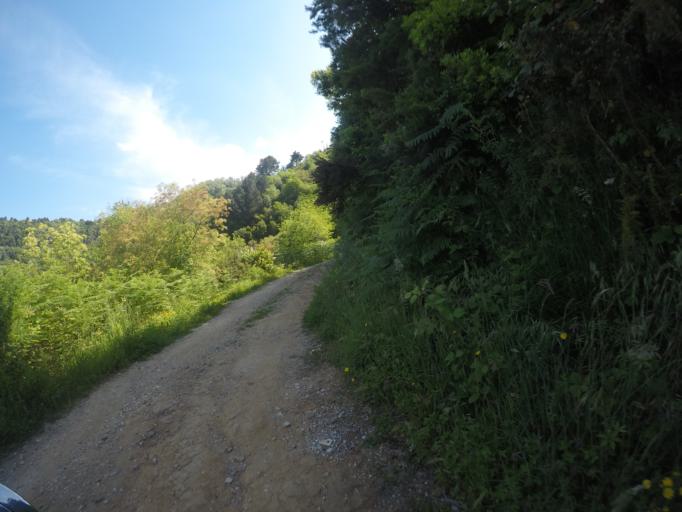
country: IT
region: Tuscany
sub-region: Provincia di Massa-Carrara
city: Massa
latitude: 44.0560
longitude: 10.1017
